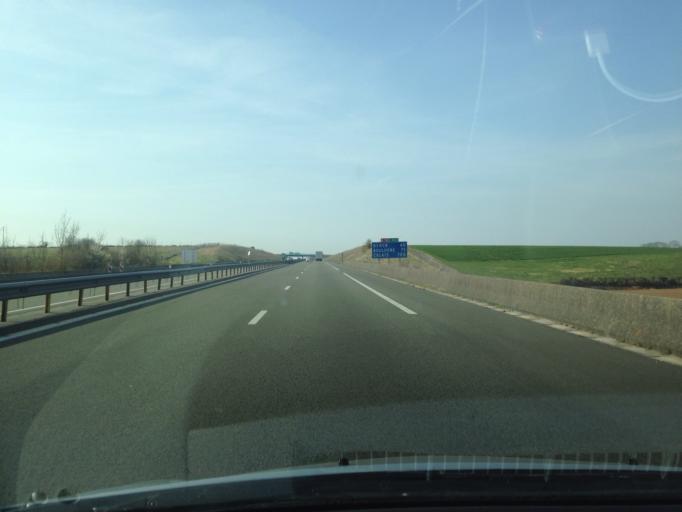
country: FR
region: Picardie
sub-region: Departement de la Somme
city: Sailly-Flibeaucourt
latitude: 50.1456
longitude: 1.8021
